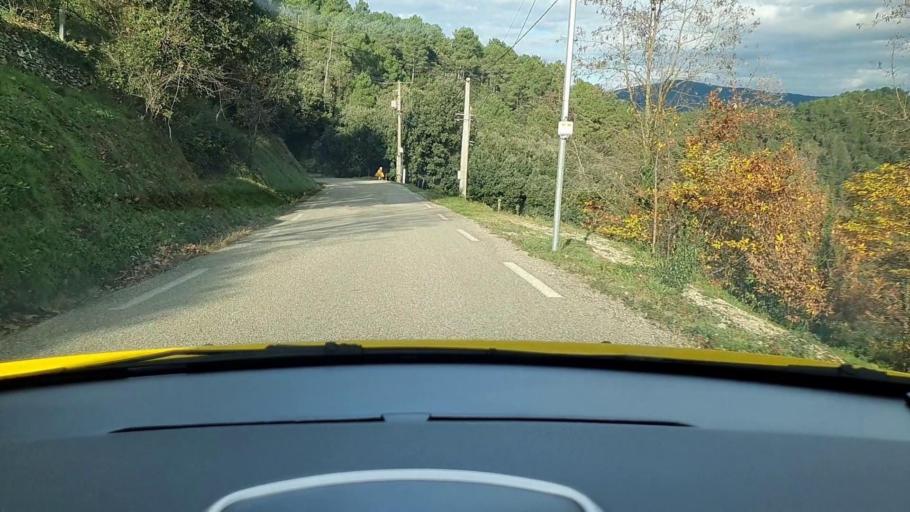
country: FR
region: Languedoc-Roussillon
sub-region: Departement du Gard
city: Branoux-les-Taillades
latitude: 44.2207
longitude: 3.9855
